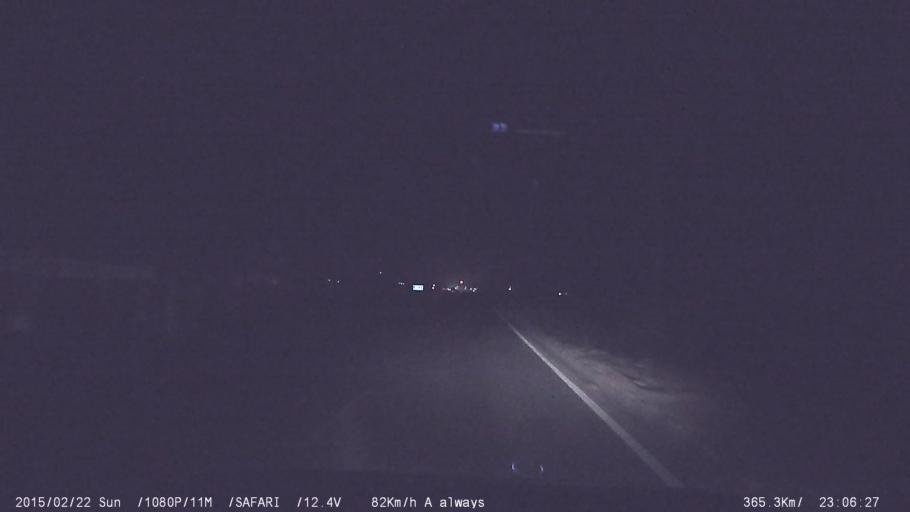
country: IN
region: Tamil Nadu
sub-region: Namakkal
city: Rasipuram
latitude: 11.4282
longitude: 78.1558
